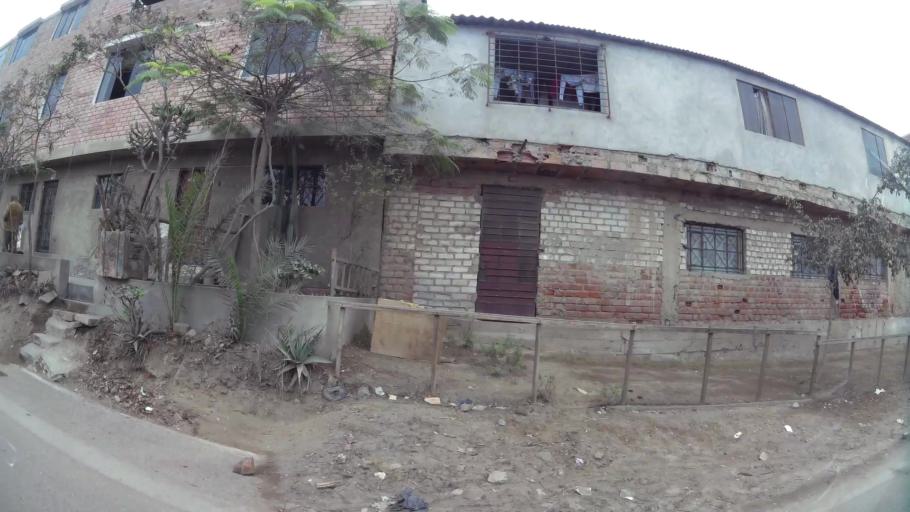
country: PE
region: Lima
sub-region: Lima
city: Surco
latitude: -12.1796
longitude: -76.9504
